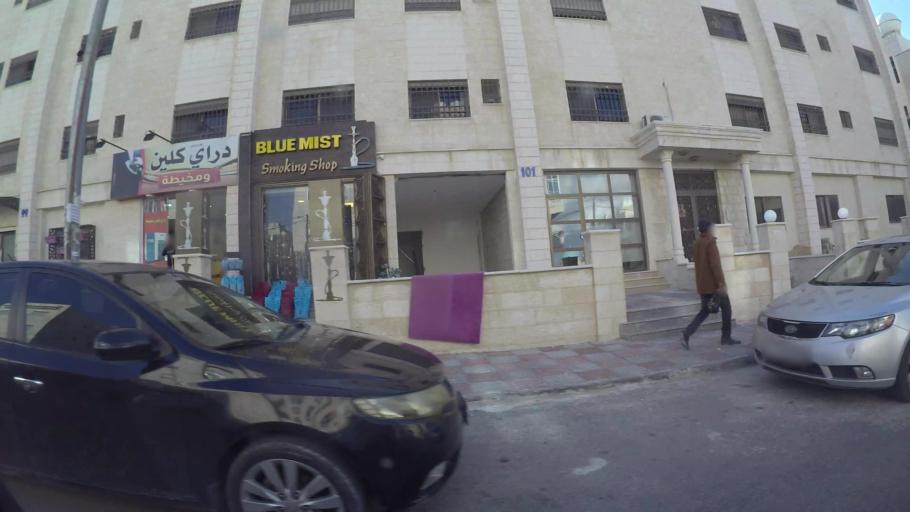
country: JO
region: Amman
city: Al Jubayhah
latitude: 32.0115
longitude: 35.8631
